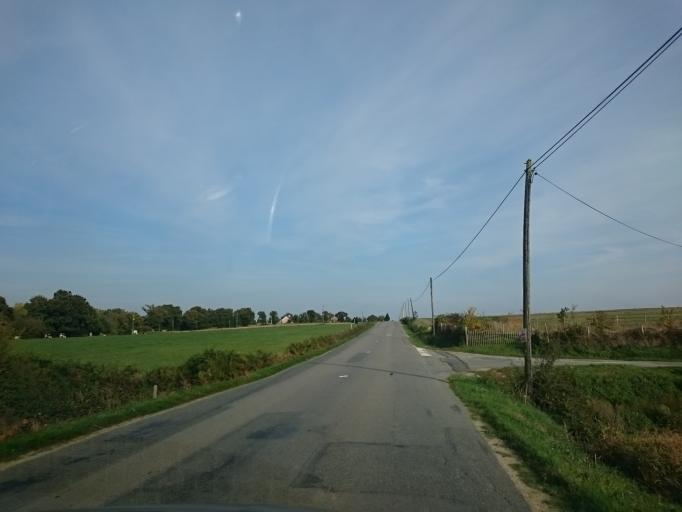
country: FR
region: Brittany
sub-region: Departement d'Ille-et-Vilaine
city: Corps-Nuds
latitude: 47.9475
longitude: -1.5823
